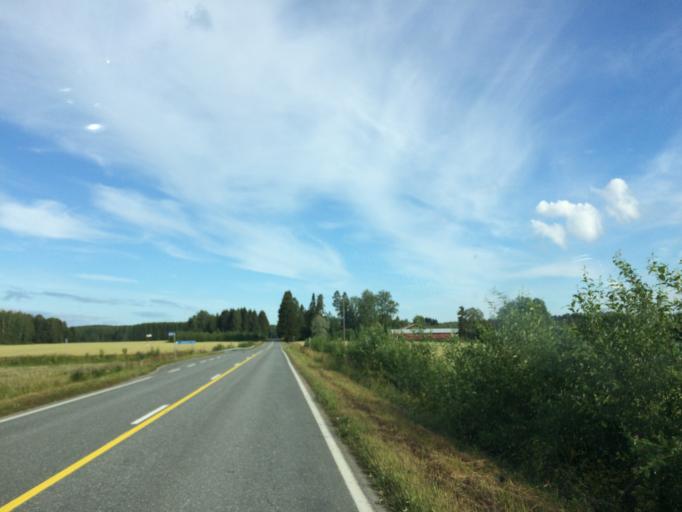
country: FI
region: Haeme
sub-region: Haemeenlinna
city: Janakkala
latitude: 60.9343
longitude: 24.5408
